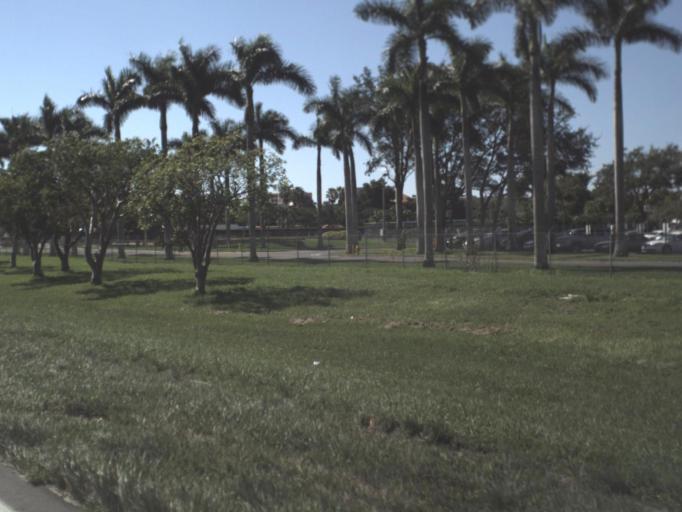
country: US
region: Florida
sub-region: Miami-Dade County
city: South Miami Heights
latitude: 25.5872
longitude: -80.3682
